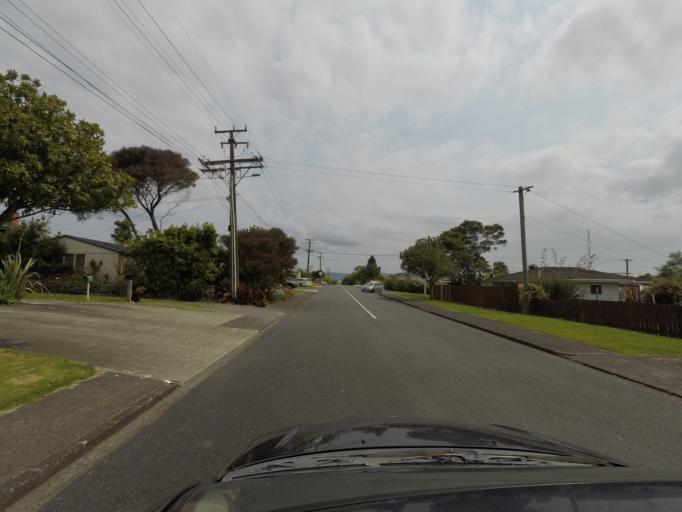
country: NZ
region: Auckland
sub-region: Auckland
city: Rosebank
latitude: -36.8413
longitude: 174.6394
